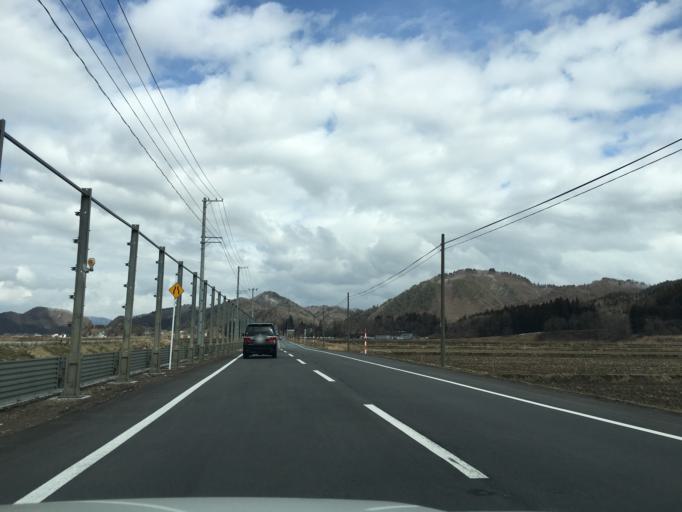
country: JP
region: Akita
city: Hanawa
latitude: 40.2252
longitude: 140.7246
